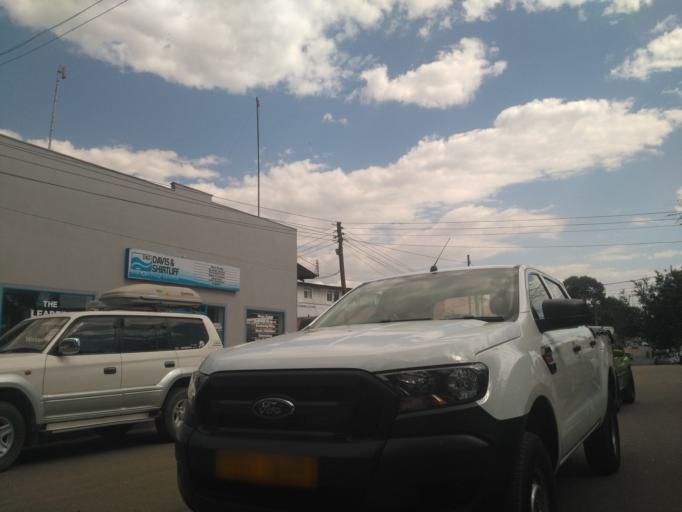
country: TZ
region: Mwanza
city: Mwanza
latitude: -2.5152
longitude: 32.9018
